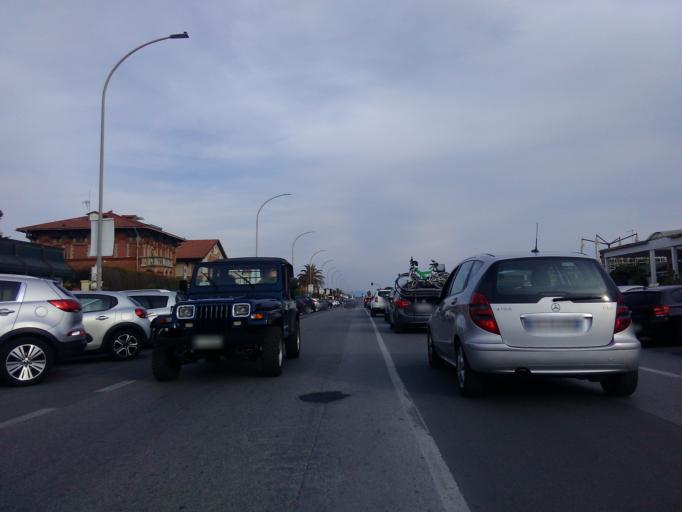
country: IT
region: Tuscany
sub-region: Provincia di Massa-Carrara
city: Massa
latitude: 44.0091
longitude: 10.0970
